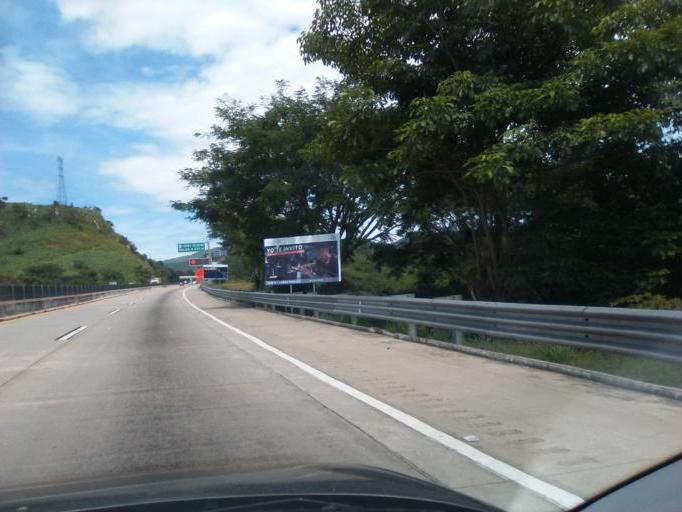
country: MX
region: Guerrero
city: Tierra Colorada
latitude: 17.1713
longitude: -99.5542
